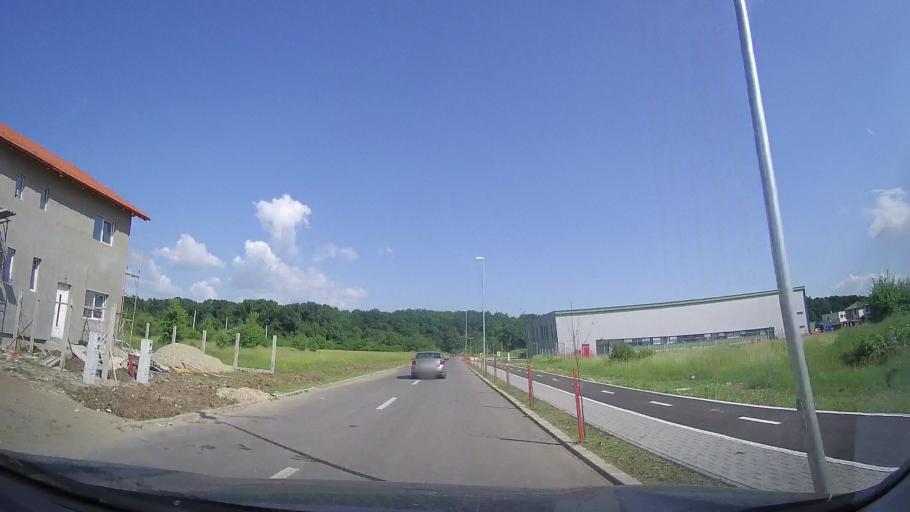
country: RO
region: Timis
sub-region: Comuna Dumbravita
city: Dumbravita
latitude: 45.7985
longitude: 21.2540
